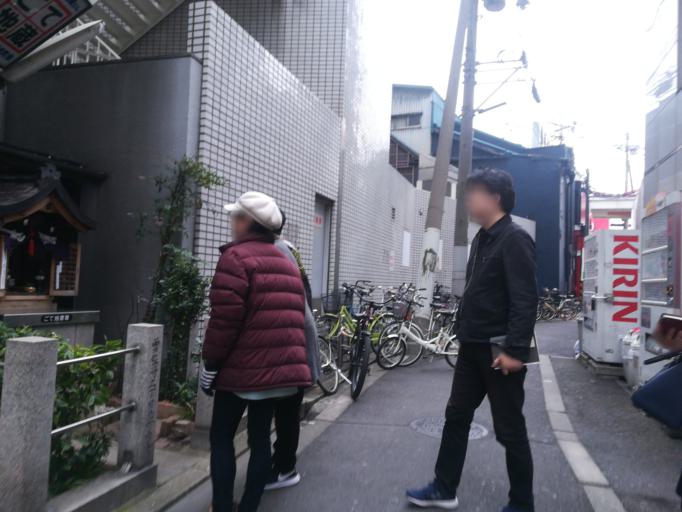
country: JP
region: Osaka
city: Osaka-shi
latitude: 34.7013
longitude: 135.5000
